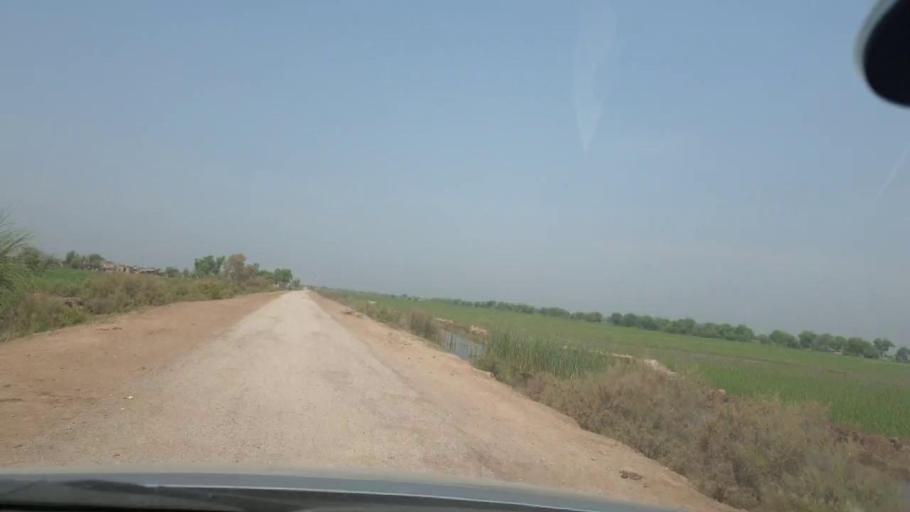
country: PK
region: Balochistan
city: Mehrabpur
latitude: 28.0652
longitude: 68.0617
